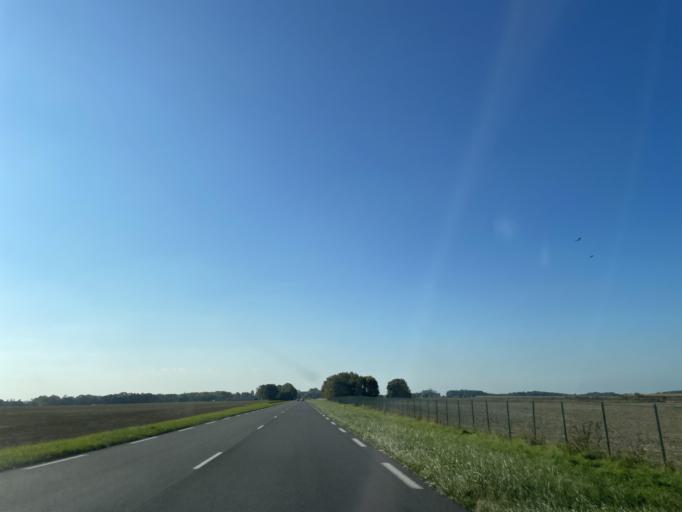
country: FR
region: Ile-de-France
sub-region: Departement de Seine-et-Marne
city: Pommeuse
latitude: 48.8338
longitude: 2.9994
